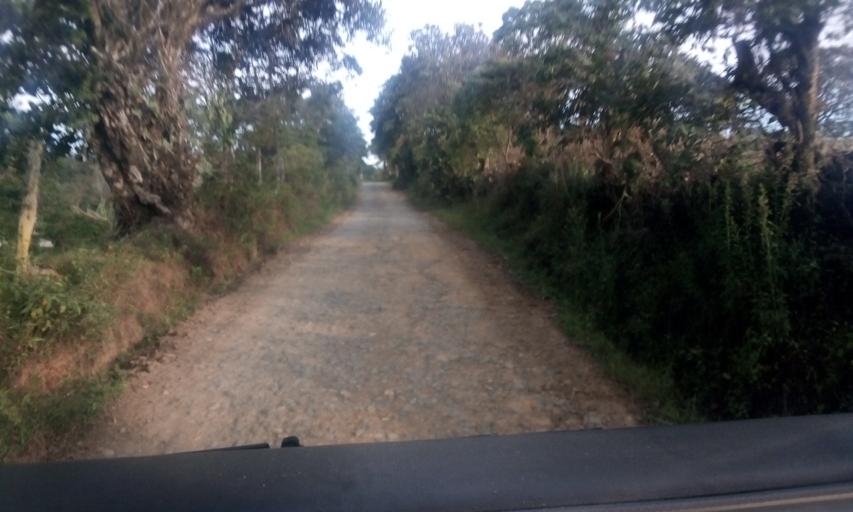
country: CO
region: Boyaca
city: Santana
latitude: 6.0141
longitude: -73.5106
